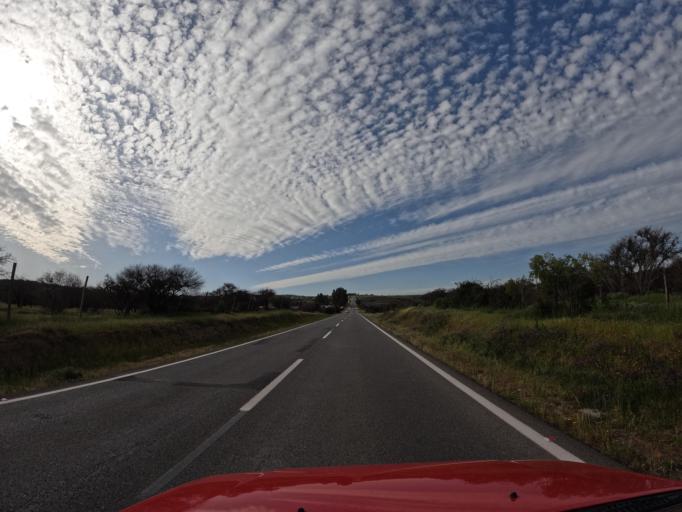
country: CL
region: O'Higgins
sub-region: Provincia de Colchagua
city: Santa Cruz
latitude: -34.2823
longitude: -71.7296
